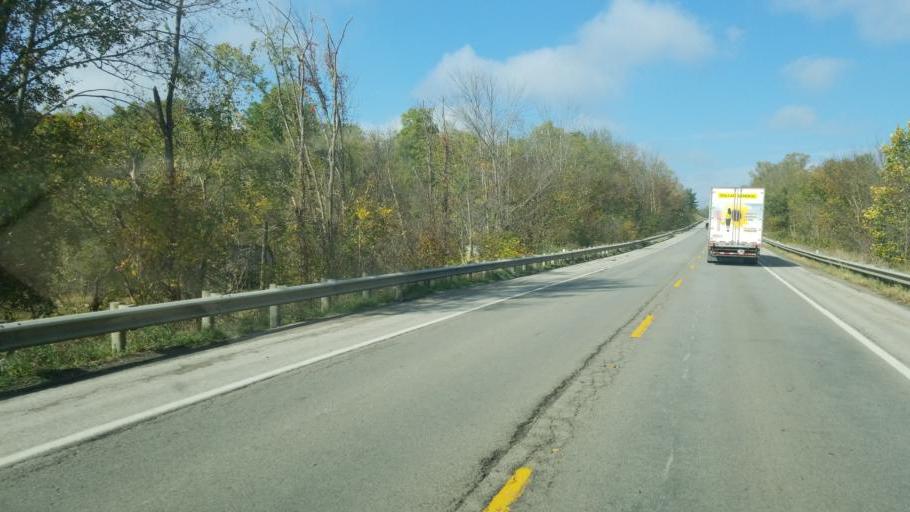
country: US
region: Ohio
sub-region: Stark County
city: Brewster
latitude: 40.6718
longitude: -81.6563
